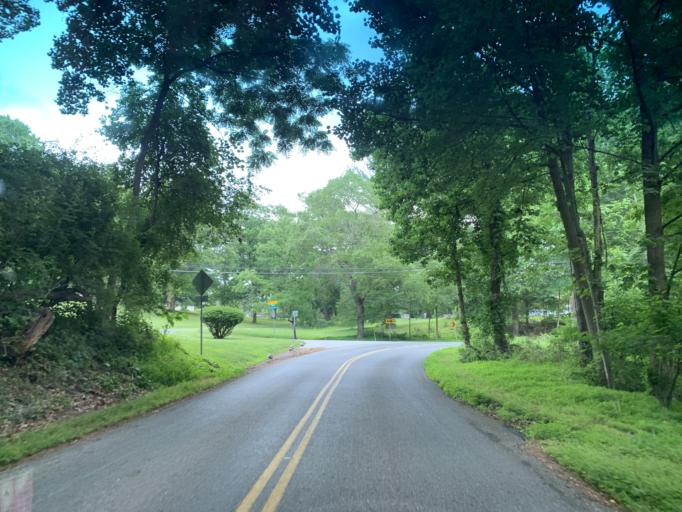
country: US
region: Maryland
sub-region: Harford County
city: Fallston
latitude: 39.5295
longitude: -76.4117
